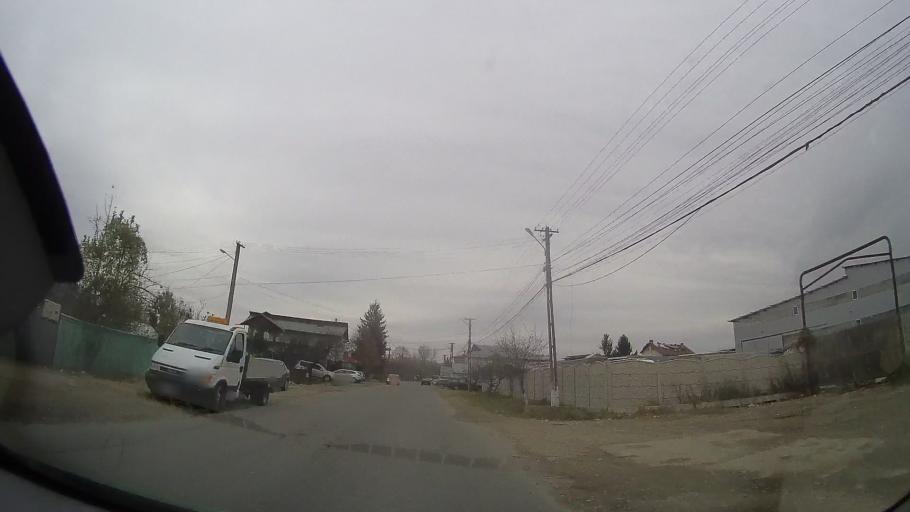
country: RO
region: Prahova
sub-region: Oras Urlati
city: Urlati
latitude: 45.0141
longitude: 26.2289
